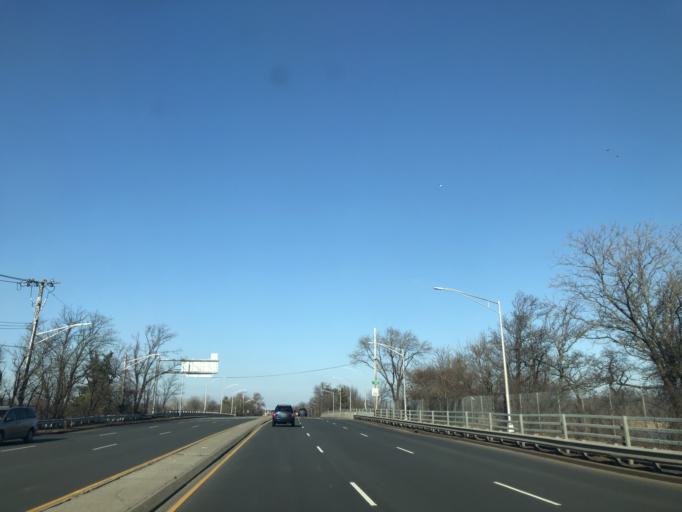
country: US
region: New York
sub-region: Richmond County
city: Staten Island
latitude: 40.5650
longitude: -74.1696
